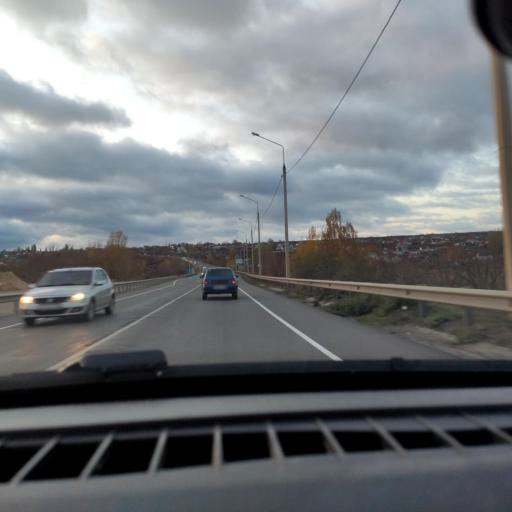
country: RU
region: Voronezj
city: Pridonskoy
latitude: 51.7248
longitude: 39.0597
